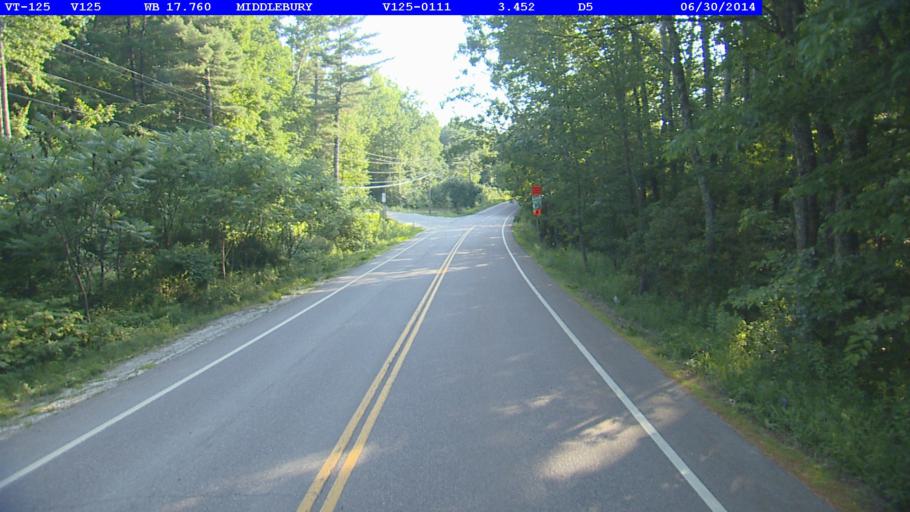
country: US
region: Vermont
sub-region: Addison County
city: Middlebury (village)
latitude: 43.9715
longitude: -73.0745
